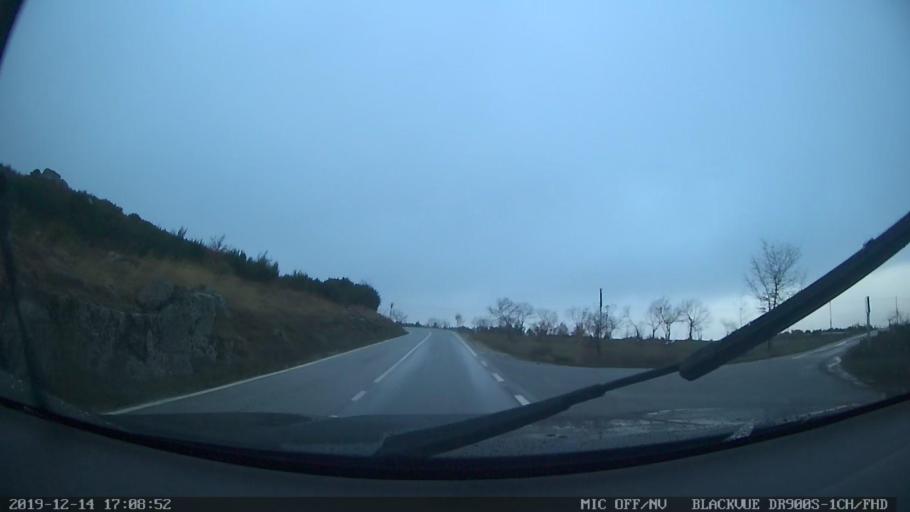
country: PT
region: Vila Real
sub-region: Vila Pouca de Aguiar
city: Vila Pouca de Aguiar
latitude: 41.4719
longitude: -7.6046
